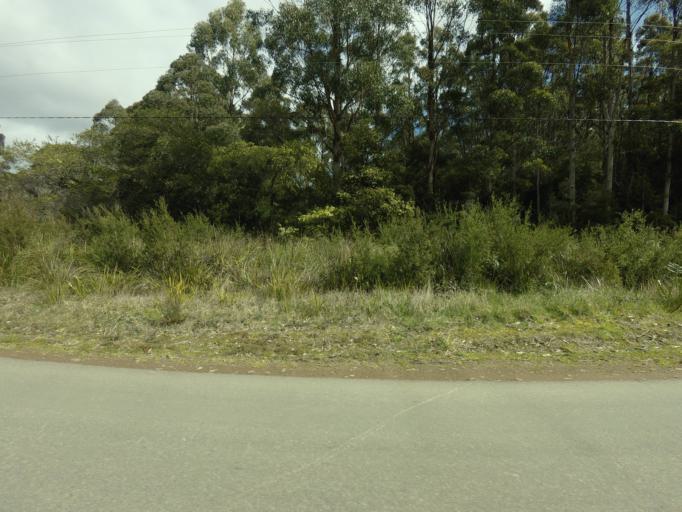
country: AU
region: Tasmania
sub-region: Huon Valley
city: Geeveston
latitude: -43.4224
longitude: 146.9723
